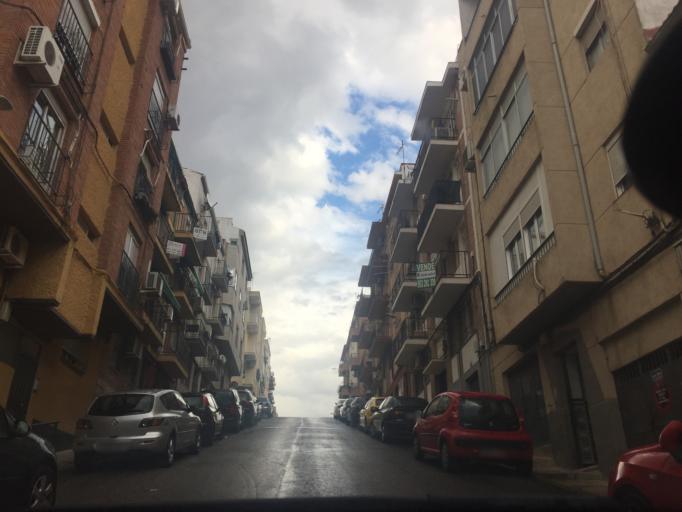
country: ES
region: Andalusia
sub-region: Provincia de Jaen
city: Jaen
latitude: 37.7753
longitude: -3.7844
